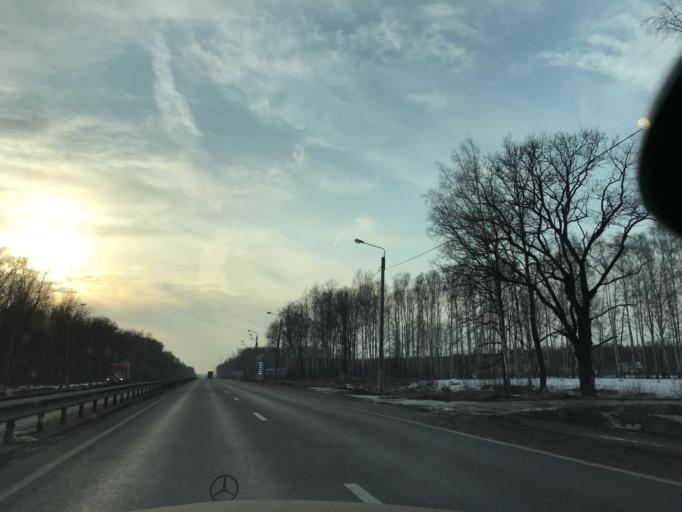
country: RU
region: Vladimir
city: Kosterevo
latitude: 55.9604
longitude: 39.6918
